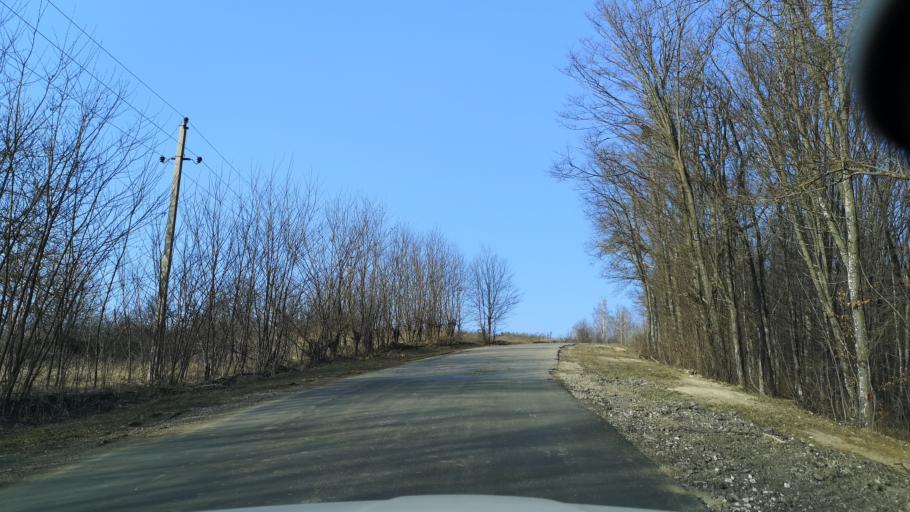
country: MD
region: Nisporeni
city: Nisporeni
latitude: 47.0901
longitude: 28.3162
